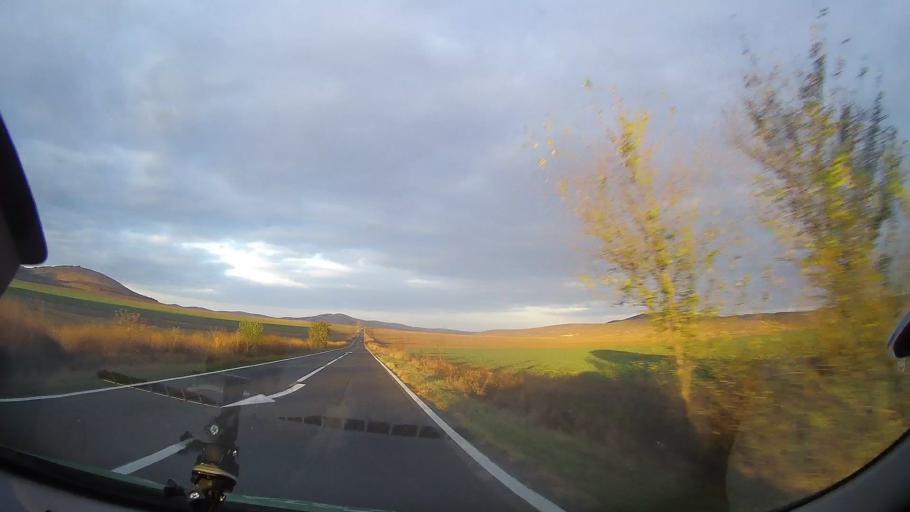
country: RO
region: Tulcea
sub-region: Comuna Nalbant
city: Nicolae Balcescu
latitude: 44.9706
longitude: 28.5392
